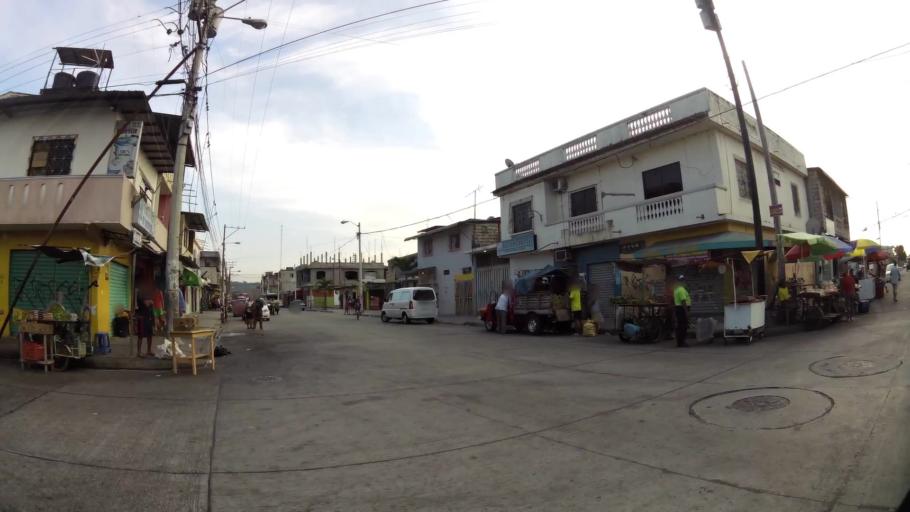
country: EC
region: Guayas
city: Eloy Alfaro
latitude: -2.0904
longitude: -79.9040
